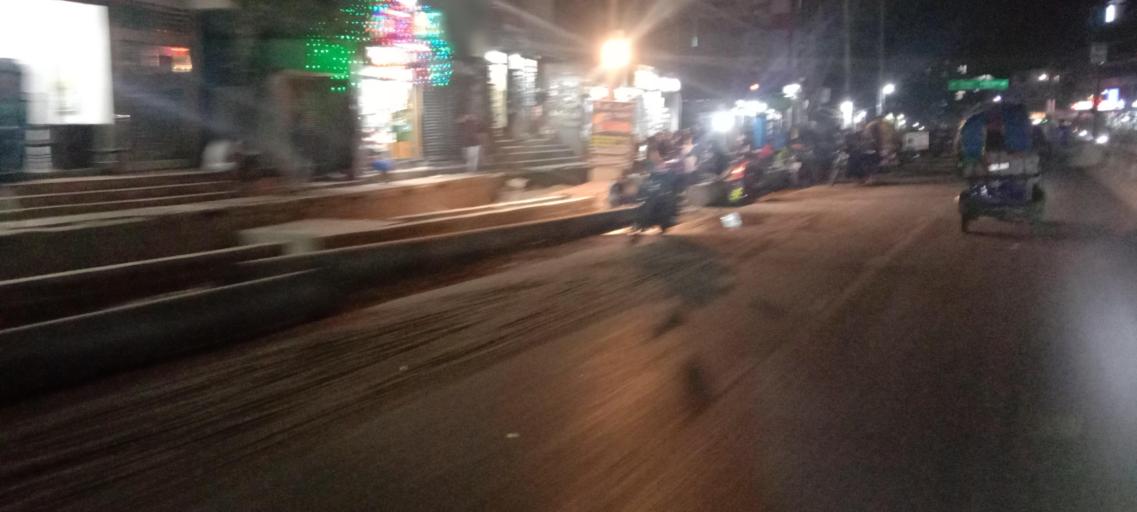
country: BD
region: Dhaka
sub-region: Dhaka
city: Dhaka
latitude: 23.7021
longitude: 90.3910
